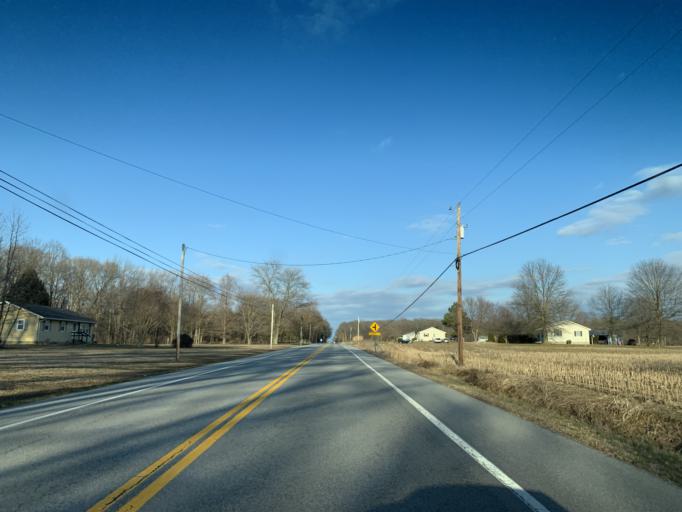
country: US
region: Maryland
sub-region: Queen Anne's County
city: Kingstown
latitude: 39.1636
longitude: -75.9381
